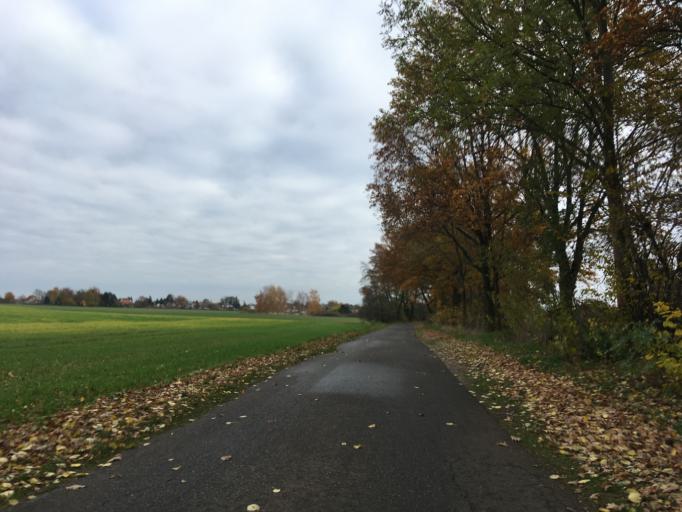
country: DE
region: Brandenburg
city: Drehnow
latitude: 51.8607
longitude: 14.3856
